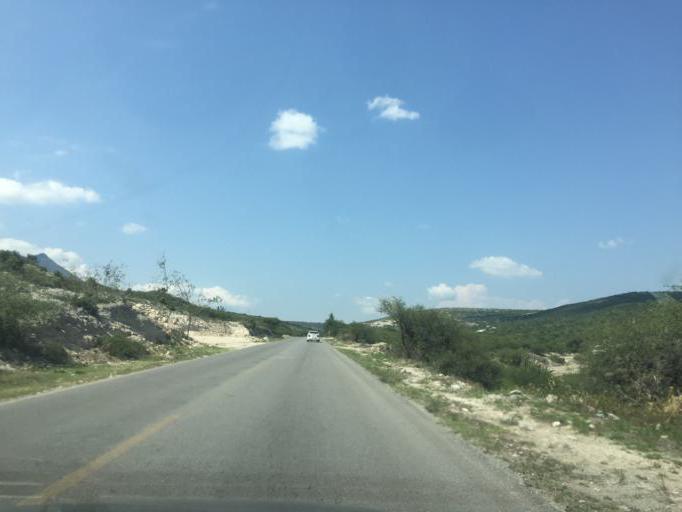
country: MX
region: Hidalgo
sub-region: Cardonal
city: Pozuelos
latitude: 20.5969
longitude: -99.1176
